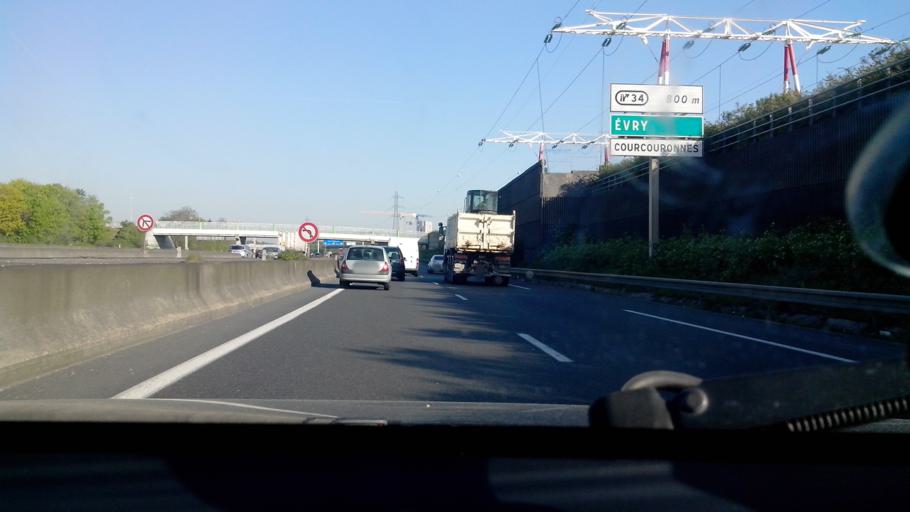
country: FR
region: Ile-de-France
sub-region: Departement de l'Essonne
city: Lisses
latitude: 48.6148
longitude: 2.4303
